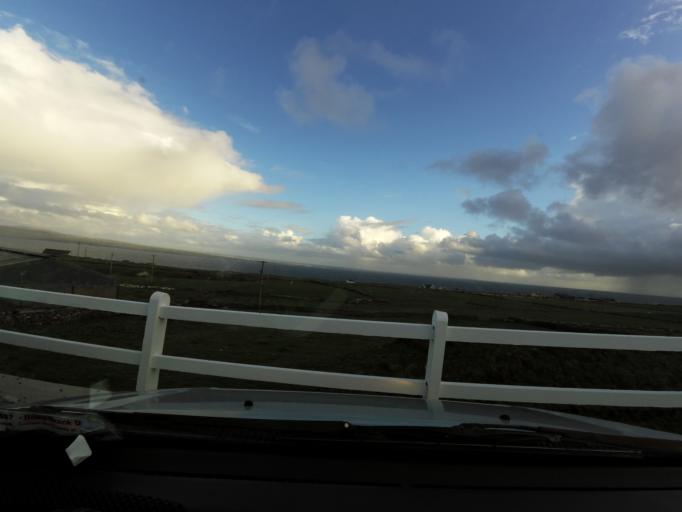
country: IE
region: Munster
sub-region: An Clar
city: Kilrush
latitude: 52.9433
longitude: -9.4543
